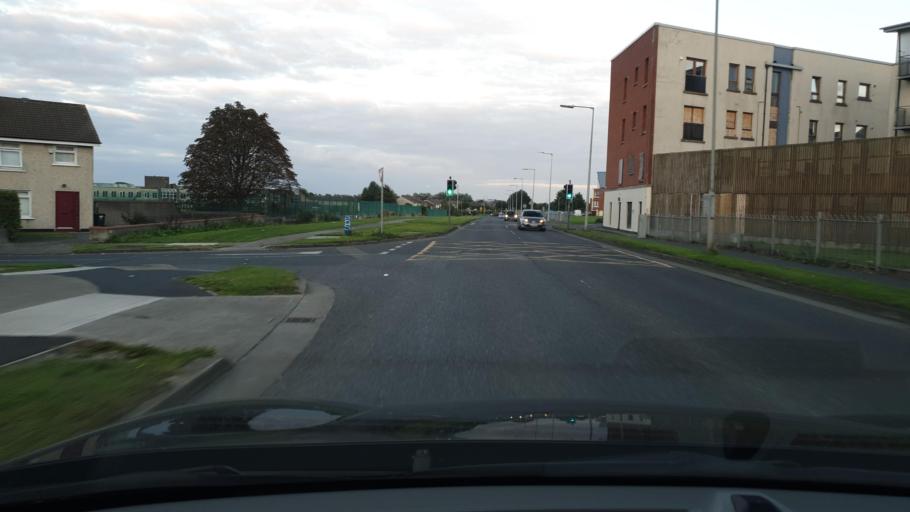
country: IE
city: Jobstown
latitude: 53.2855
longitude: -6.4148
